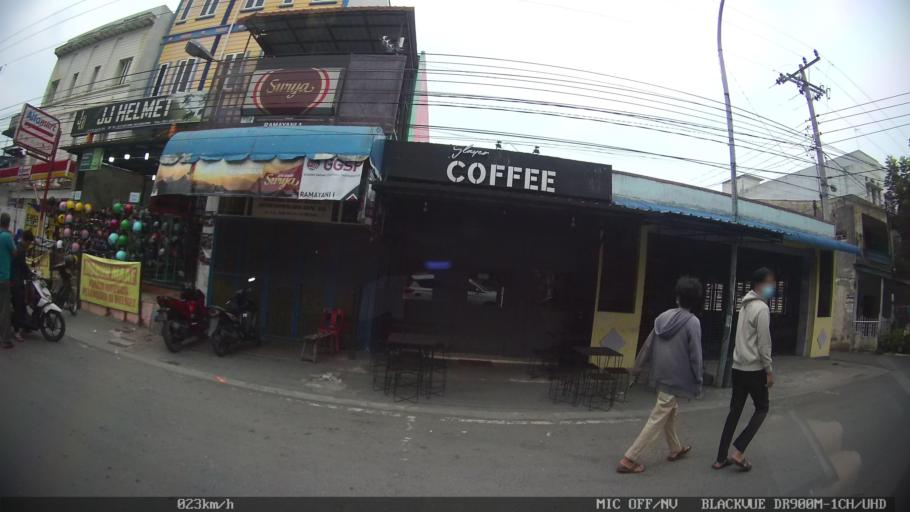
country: ID
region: North Sumatra
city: Medan
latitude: 3.5686
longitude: 98.6967
